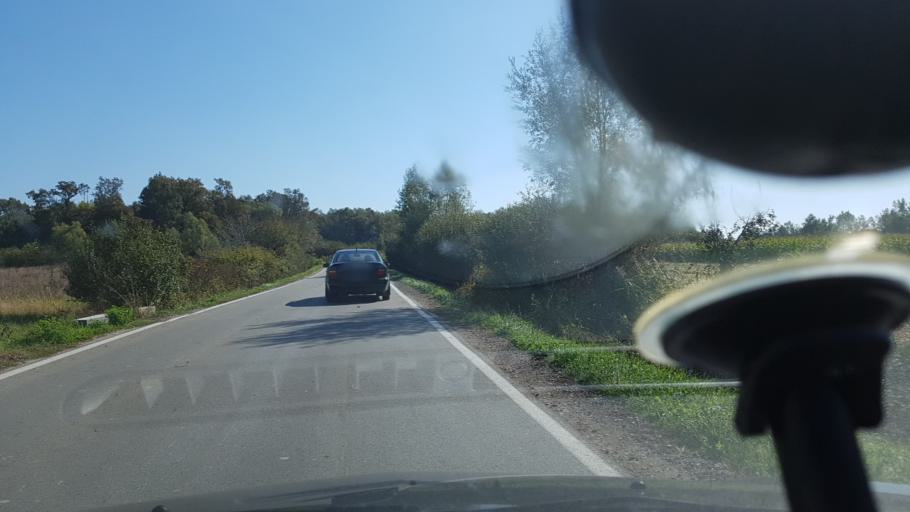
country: HR
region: Zagrebacka
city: Lupoglav
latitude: 45.7332
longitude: 16.3017
